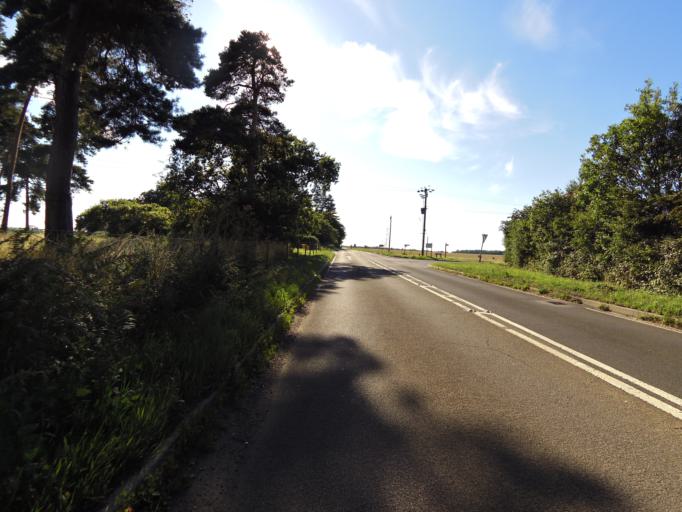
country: GB
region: England
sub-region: Suffolk
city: Kesgrave
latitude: 52.0508
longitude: 1.2544
